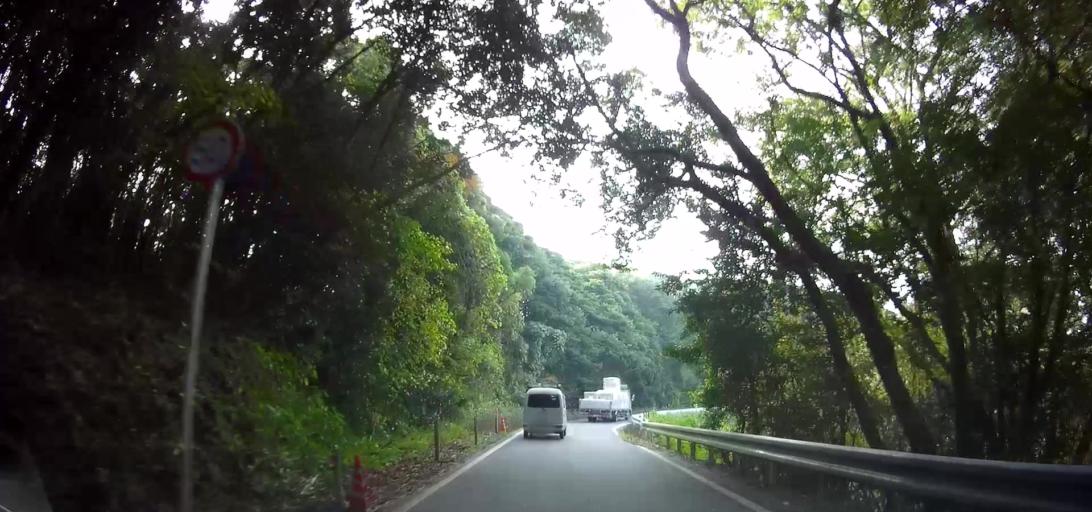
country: JP
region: Nagasaki
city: Shimabara
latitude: 32.6789
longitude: 130.1964
